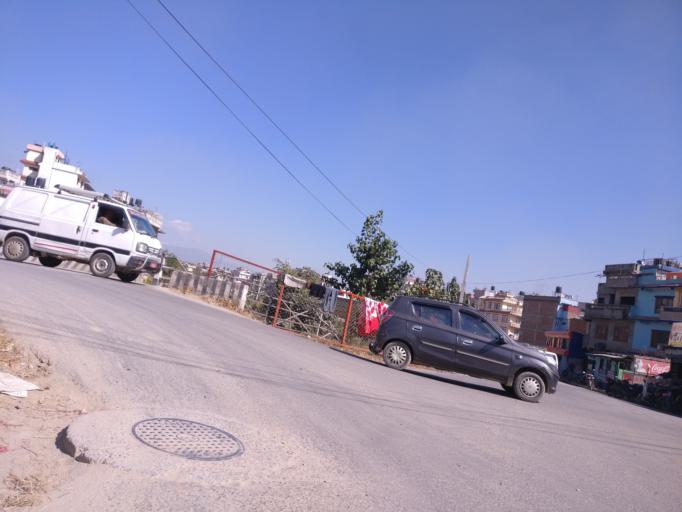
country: NP
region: Central Region
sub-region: Bagmati Zone
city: Patan
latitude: 27.6790
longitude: 85.3353
